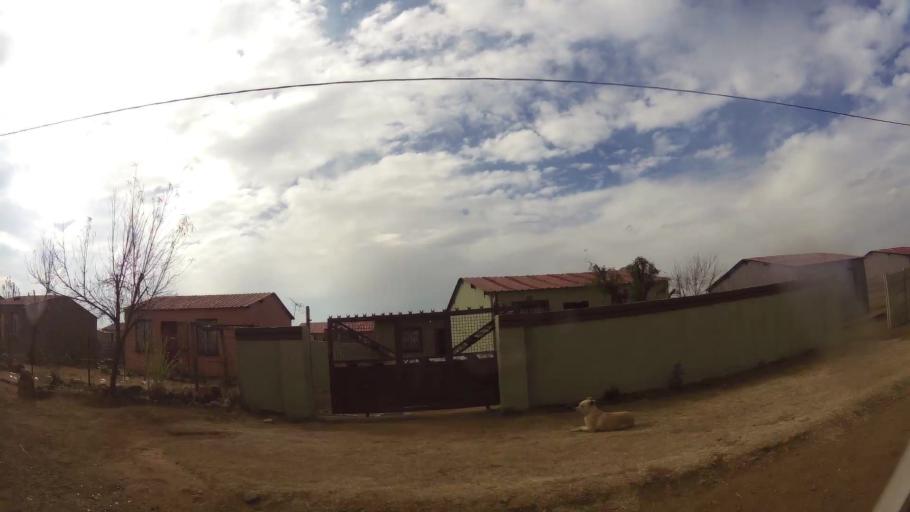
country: ZA
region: Gauteng
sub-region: Ekurhuleni Metropolitan Municipality
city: Germiston
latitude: -26.4115
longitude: 28.1624
